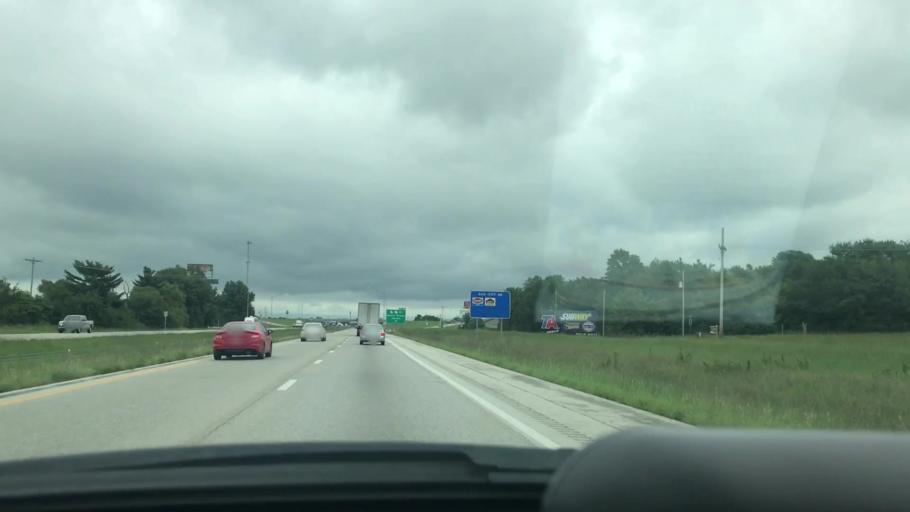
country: US
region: Missouri
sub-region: Lawrence County
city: Mount Vernon
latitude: 37.0891
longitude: -93.8116
